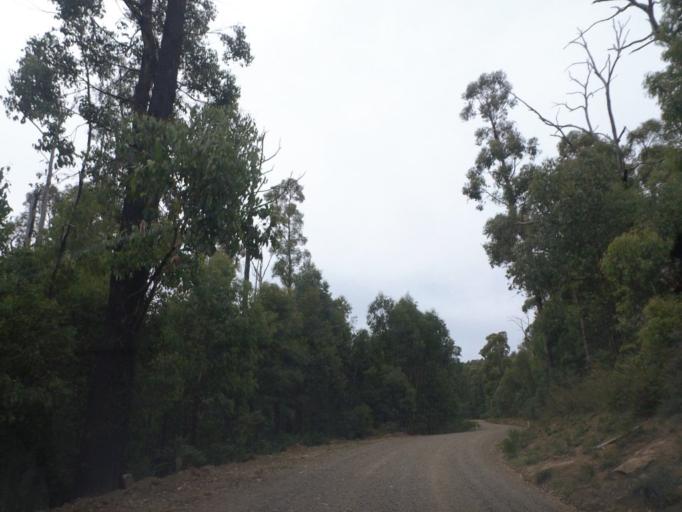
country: AU
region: Victoria
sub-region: Yarra Ranges
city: Healesville
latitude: -37.4206
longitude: 145.5848
